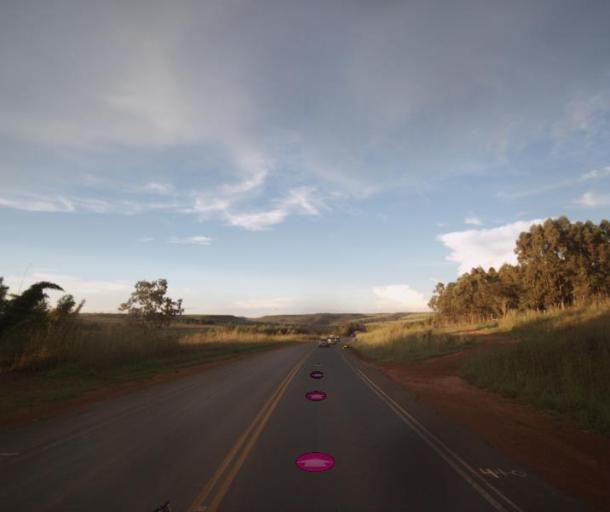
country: BR
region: Goias
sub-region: Anapolis
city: Anapolis
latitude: -16.1718
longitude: -48.8999
